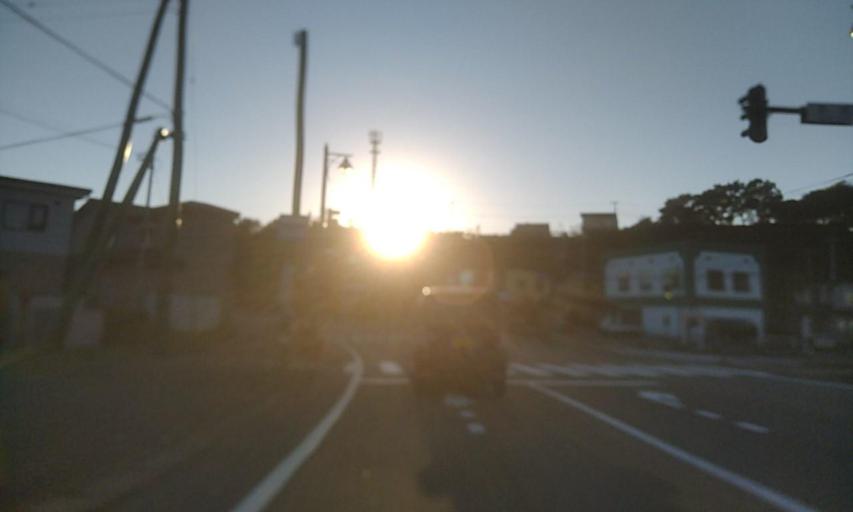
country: JP
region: Hokkaido
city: Shizunai-furukawacho
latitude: 42.1281
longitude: 142.9280
